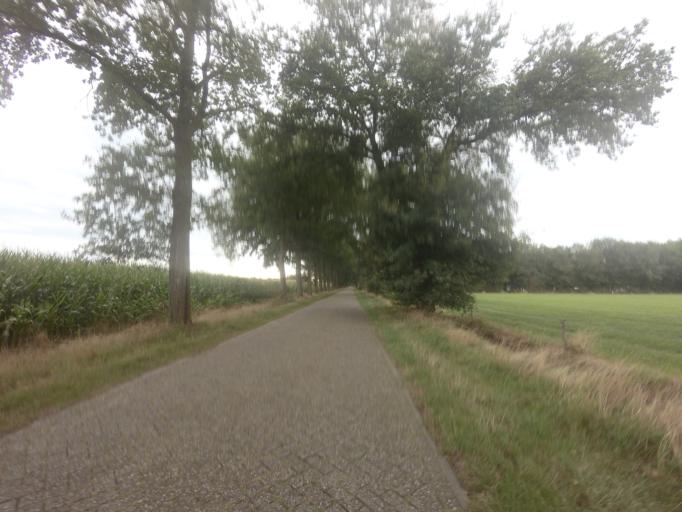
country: NL
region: Overijssel
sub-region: Gemeente Raalte
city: Raalte
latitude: 52.3414
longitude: 6.3060
